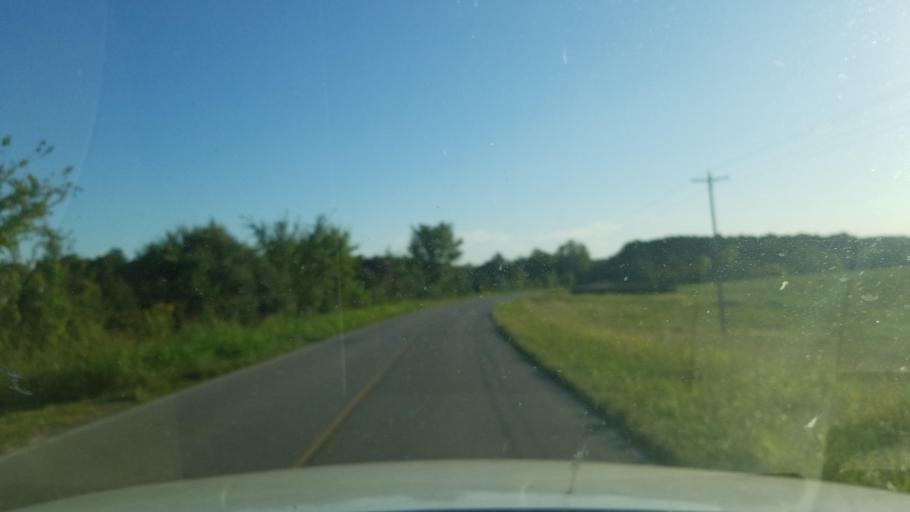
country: US
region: Illinois
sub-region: Hardin County
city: Rosiclare
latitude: 37.5700
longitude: -88.4002
